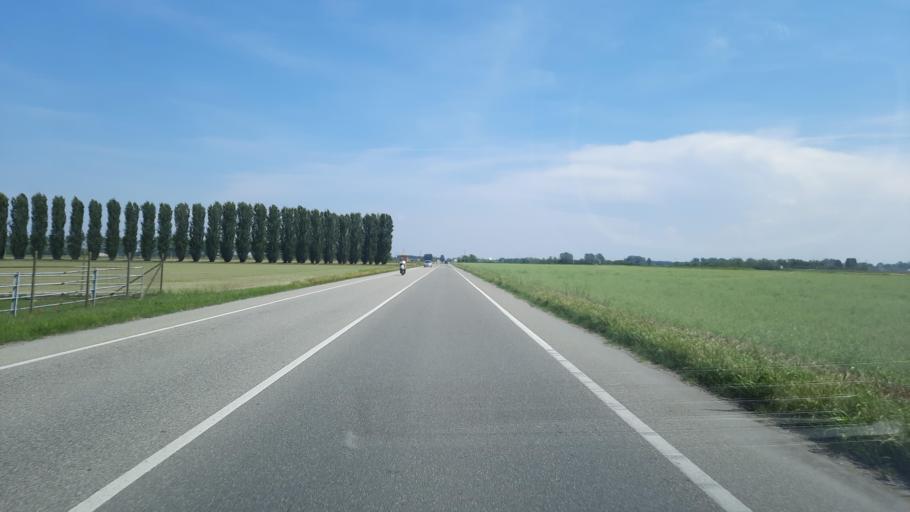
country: IT
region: Lombardy
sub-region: Provincia di Pavia
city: Mortara
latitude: 45.2463
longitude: 8.7651
